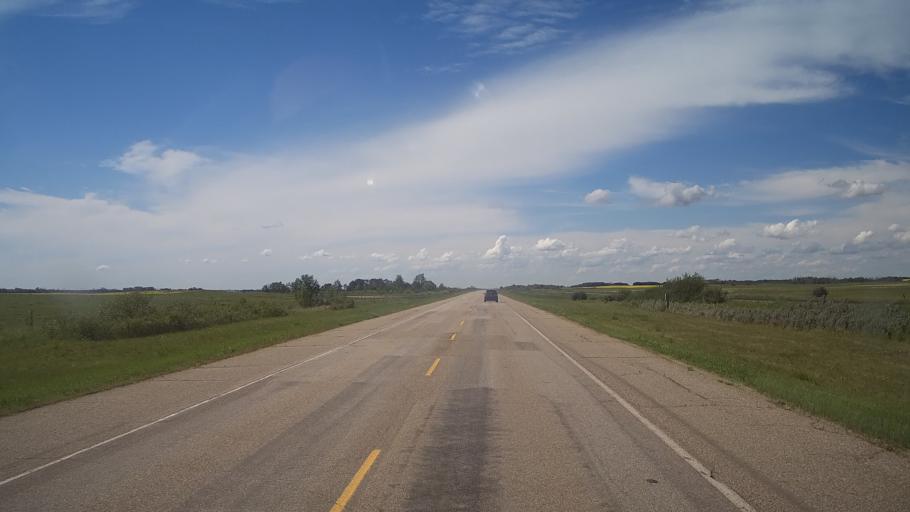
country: CA
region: Saskatchewan
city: Yorkton
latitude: 51.0683
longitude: -102.2209
